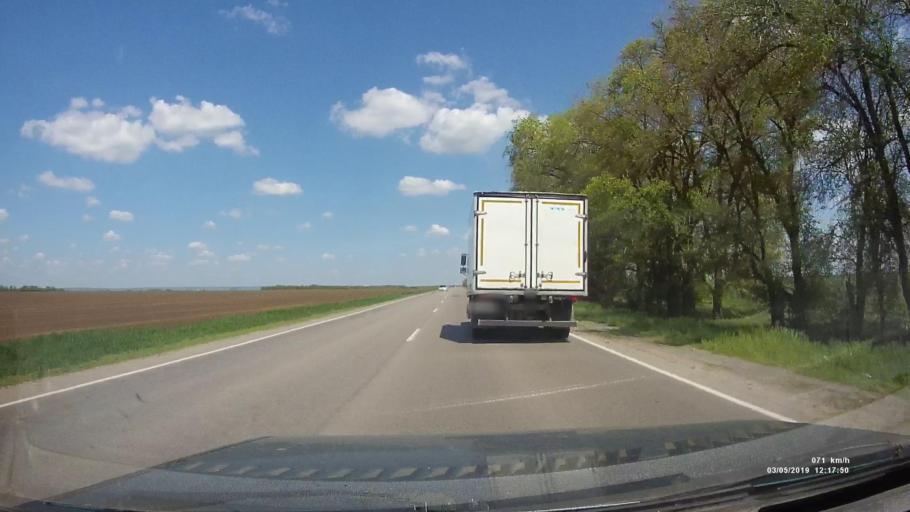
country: RU
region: Rostov
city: Melikhovskaya
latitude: 47.3866
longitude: 40.5951
